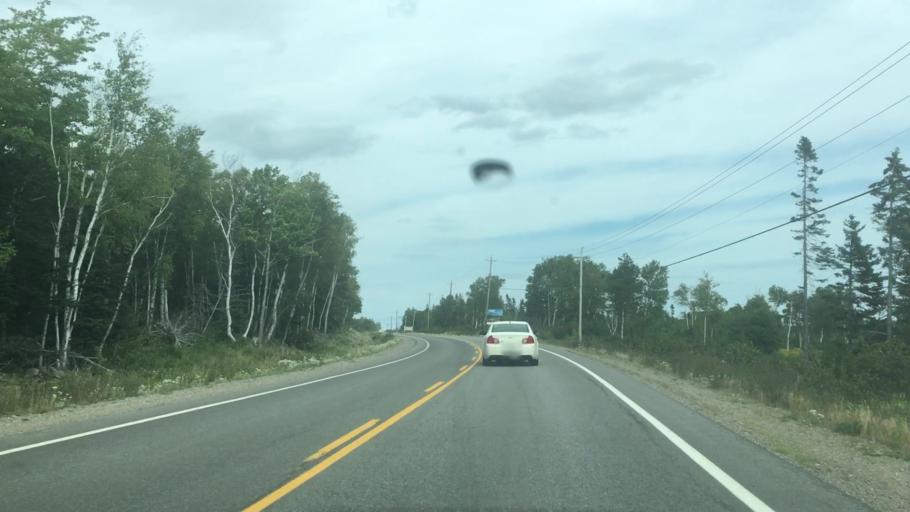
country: CA
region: Nova Scotia
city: Sydney Mines
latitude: 46.5175
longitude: -60.4252
